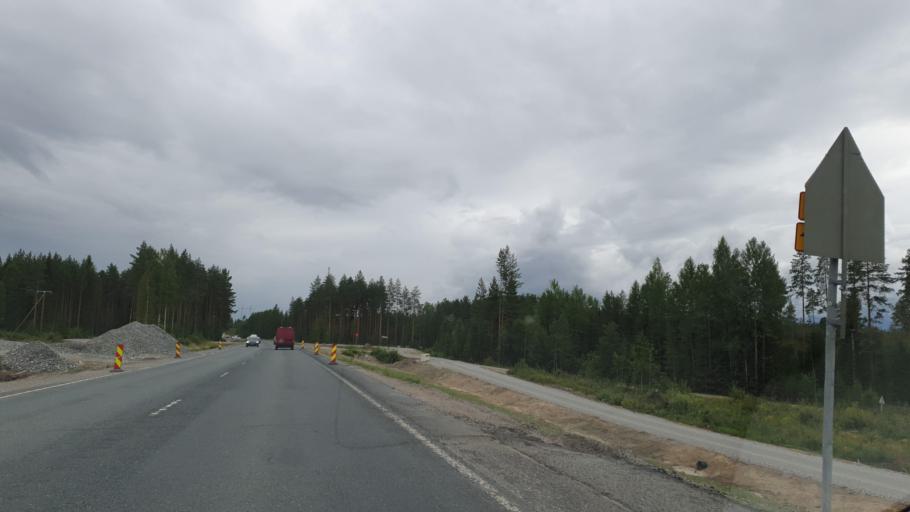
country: FI
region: Northern Savo
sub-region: Ylae-Savo
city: Lapinlahti
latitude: 63.2804
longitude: 27.4560
